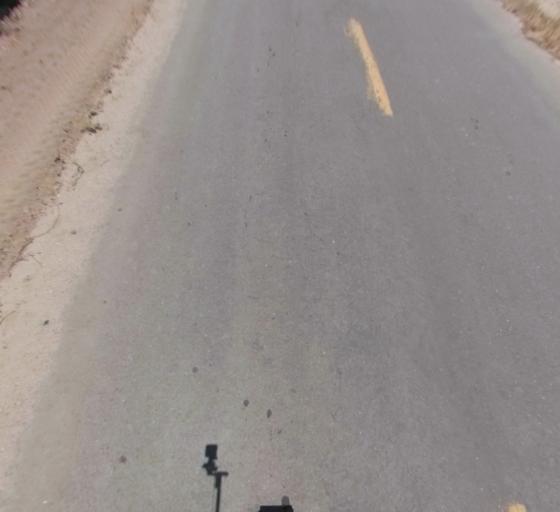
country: US
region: California
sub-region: Madera County
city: Parkwood
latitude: 36.8731
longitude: -120.0756
